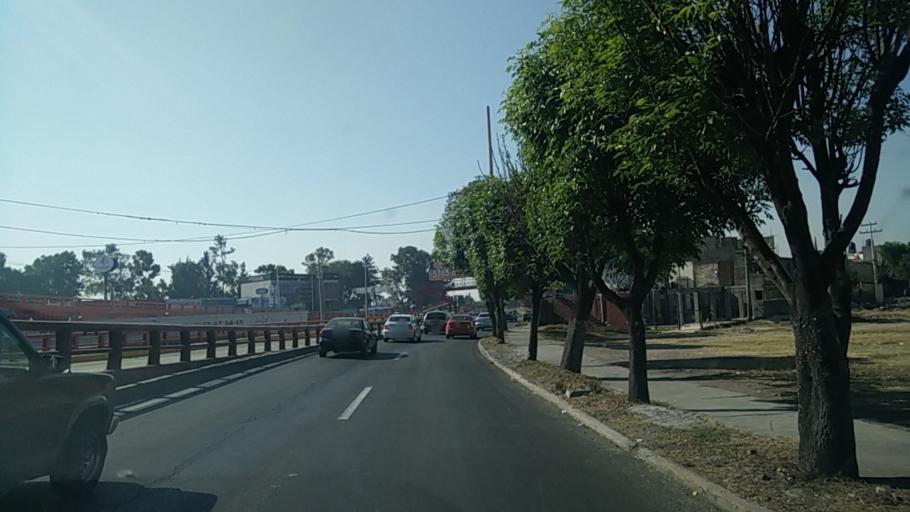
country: MX
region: Mexico
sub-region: Atenco
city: Colonia el Salado
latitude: 19.6032
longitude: -99.0153
